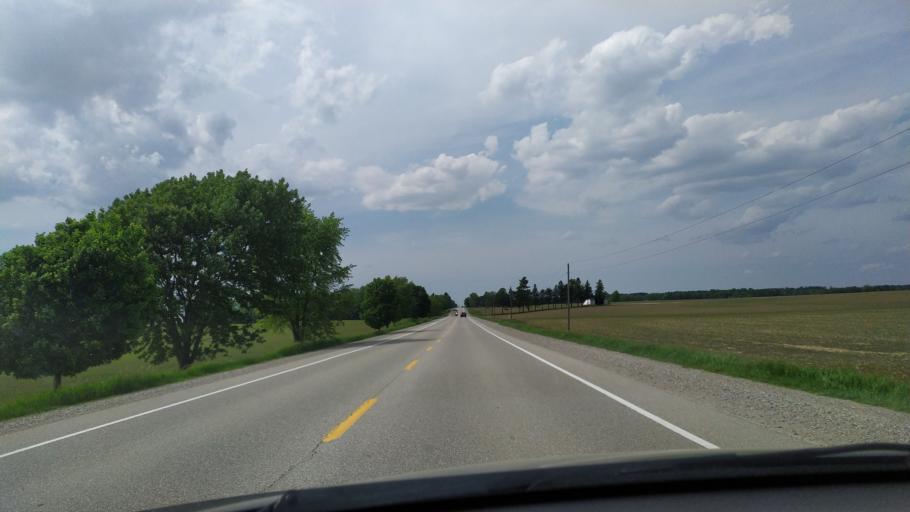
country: CA
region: Ontario
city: Dorchester
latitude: 43.1479
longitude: -81.0347
